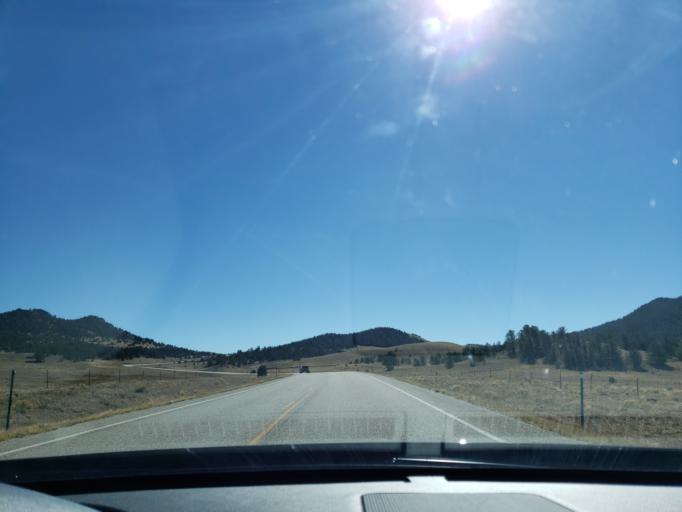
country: US
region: Colorado
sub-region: Chaffee County
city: Salida
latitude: 38.8507
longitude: -105.6510
